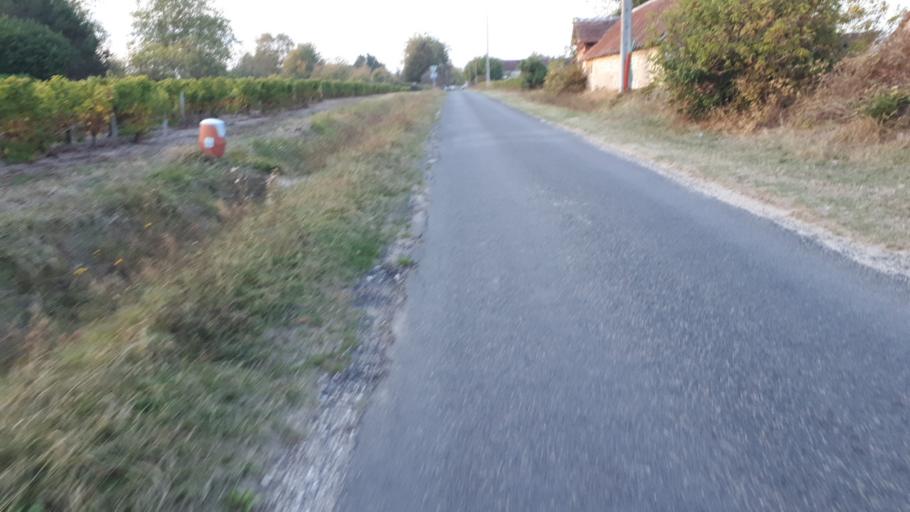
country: FR
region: Centre
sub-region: Departement du Loir-et-Cher
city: Saint-Romain-sur-Cher
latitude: 47.3617
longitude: 1.4074
